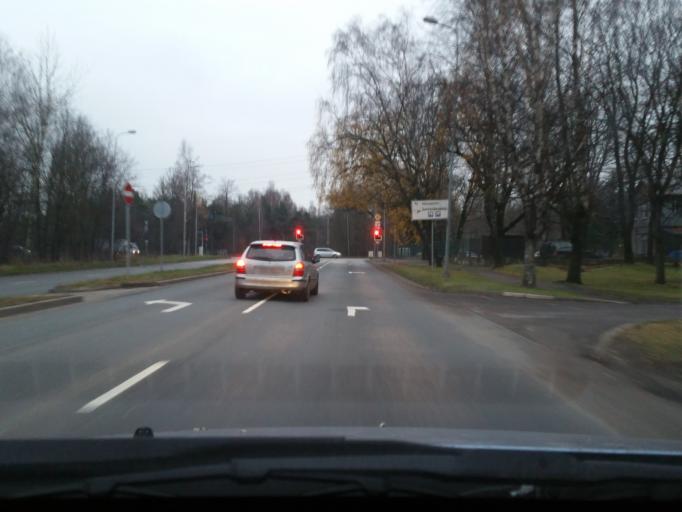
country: LV
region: Riga
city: Riga
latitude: 56.9974
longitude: 24.1334
